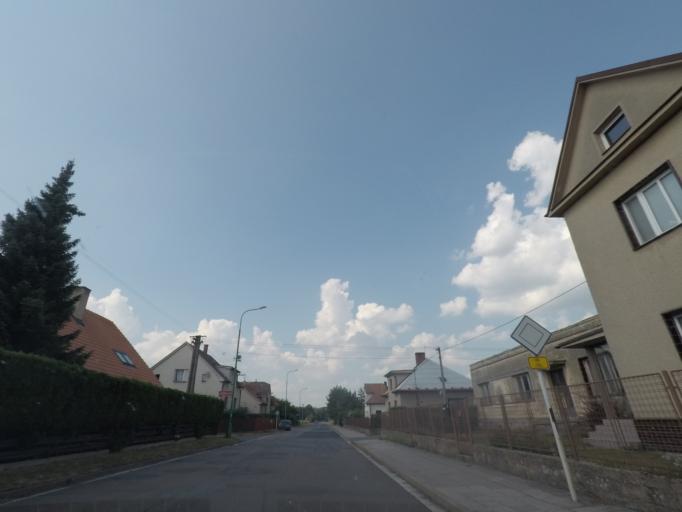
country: CZ
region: Pardubicky
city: Horni Jeleni
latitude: 50.0530
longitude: 16.0834
